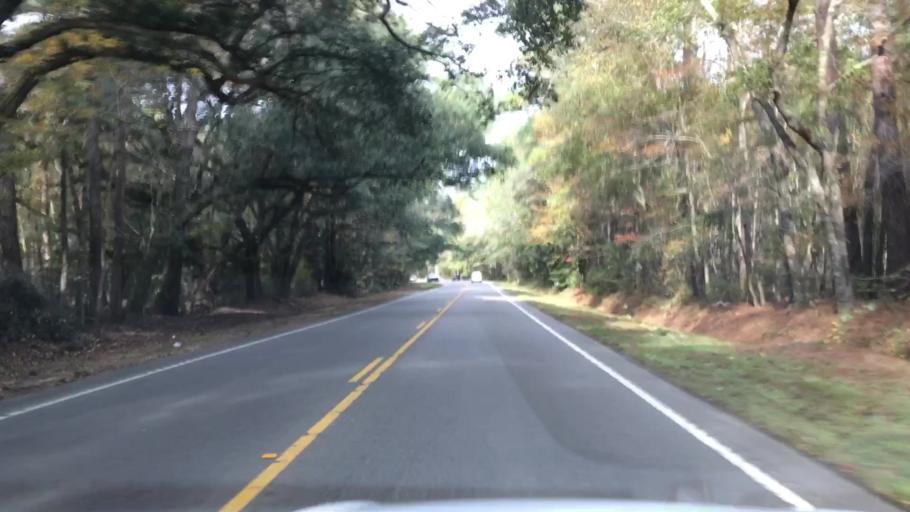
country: US
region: South Carolina
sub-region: Colleton County
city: Walterboro
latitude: 32.8326
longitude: -80.5699
